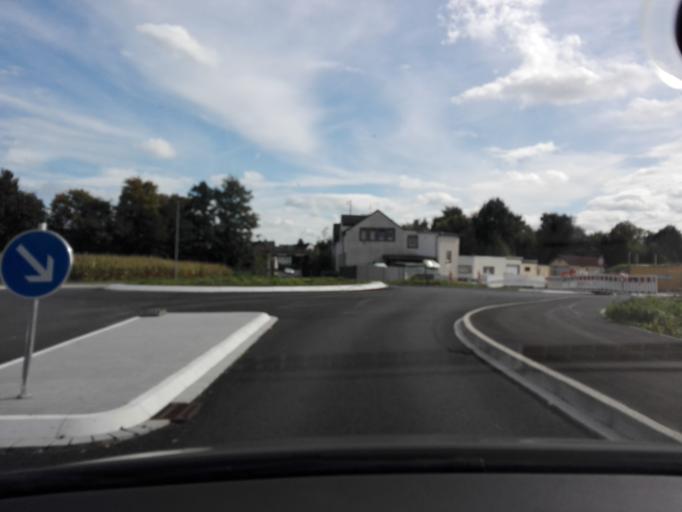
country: DE
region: North Rhine-Westphalia
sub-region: Regierungsbezirk Arnsberg
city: Unna
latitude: 51.5455
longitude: 7.6689
